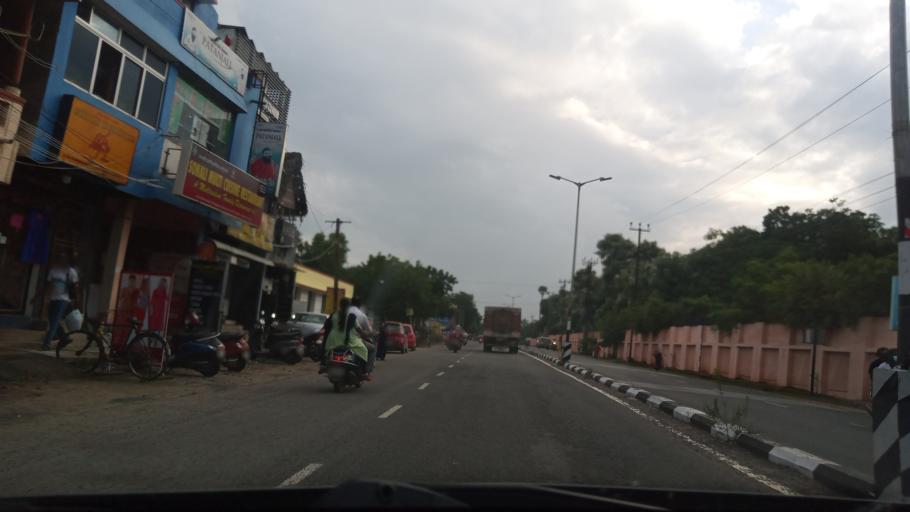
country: IN
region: Tamil Nadu
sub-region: Villupuram
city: Auroville
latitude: 12.0157
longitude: 79.8586
